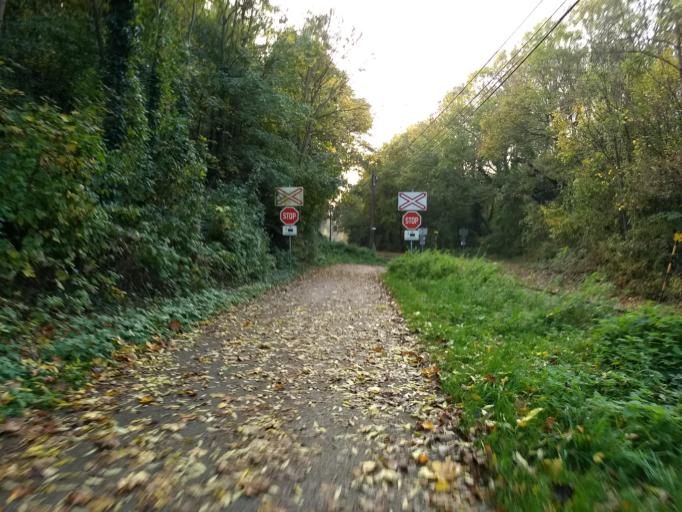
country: AT
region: Lower Austria
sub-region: Politischer Bezirk Modling
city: Perchtoldsdorf
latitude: 48.1310
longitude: 16.2447
